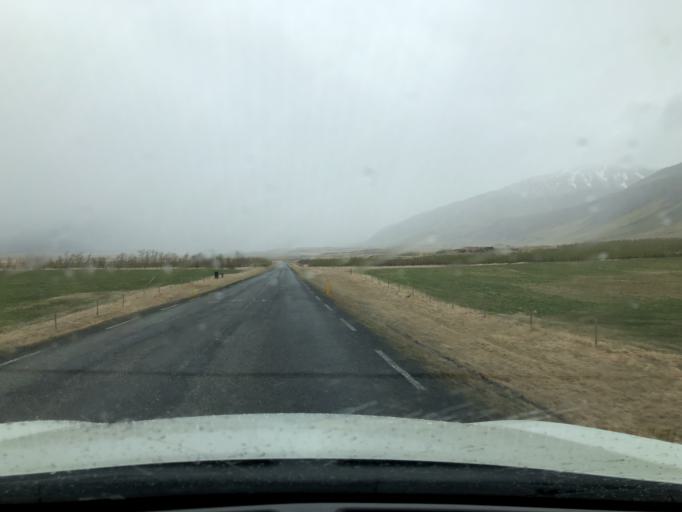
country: IS
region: East
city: Hoefn
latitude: 64.3558
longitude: -15.2577
